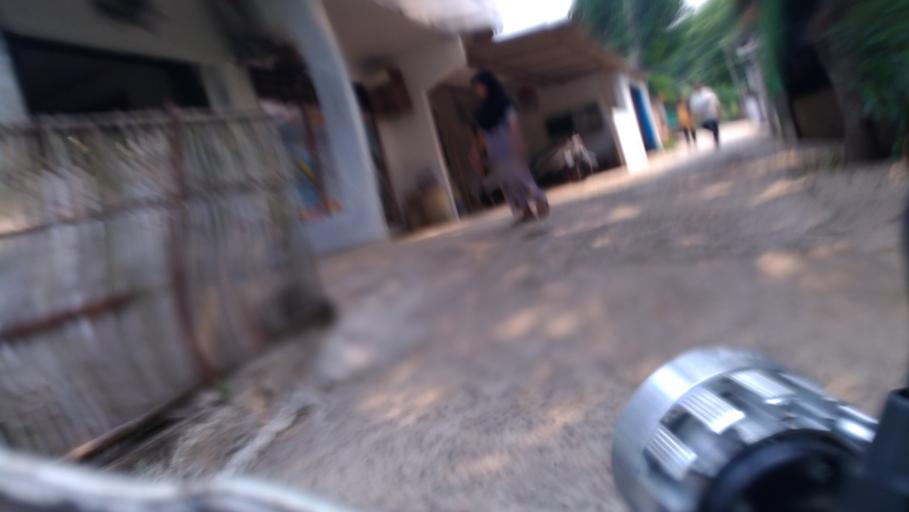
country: ID
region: West Java
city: Depok
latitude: -6.3669
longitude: 106.8771
